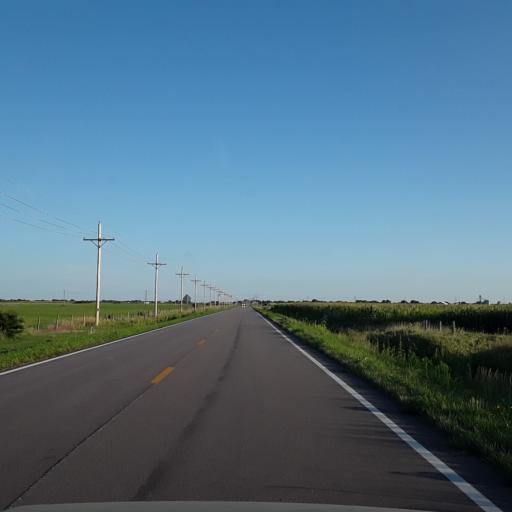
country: US
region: Nebraska
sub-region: Hall County
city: Grand Island
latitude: 40.9663
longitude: -98.3208
